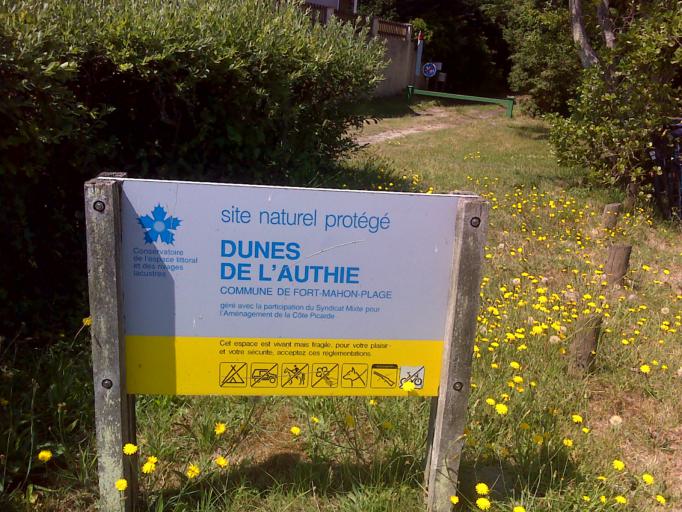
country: FR
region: Picardie
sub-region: Departement de la Somme
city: Fort-Mahon-Plage
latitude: 50.3523
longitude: 1.5716
